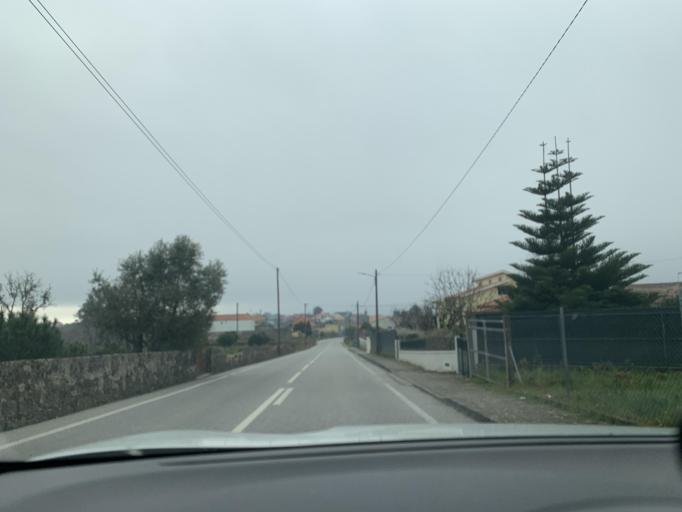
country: PT
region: Viseu
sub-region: Concelho de Tondela
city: Tondela
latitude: 40.5019
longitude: -8.0774
